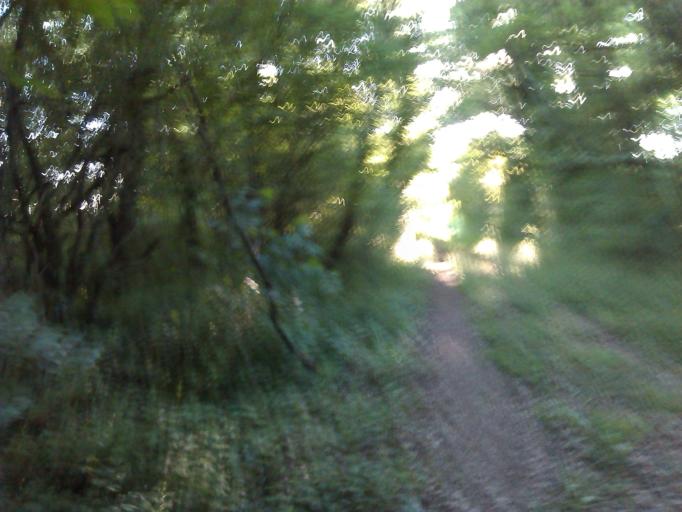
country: FR
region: Centre
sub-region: Departement de l'Indre
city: Le Blanc
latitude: 46.5998
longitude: 0.9837
